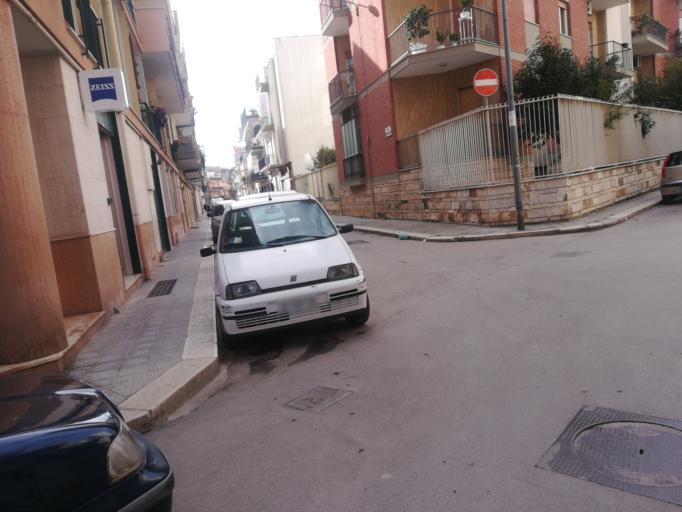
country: IT
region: Apulia
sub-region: Provincia di Barletta - Andria - Trani
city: Andria
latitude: 41.2251
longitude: 16.3047
